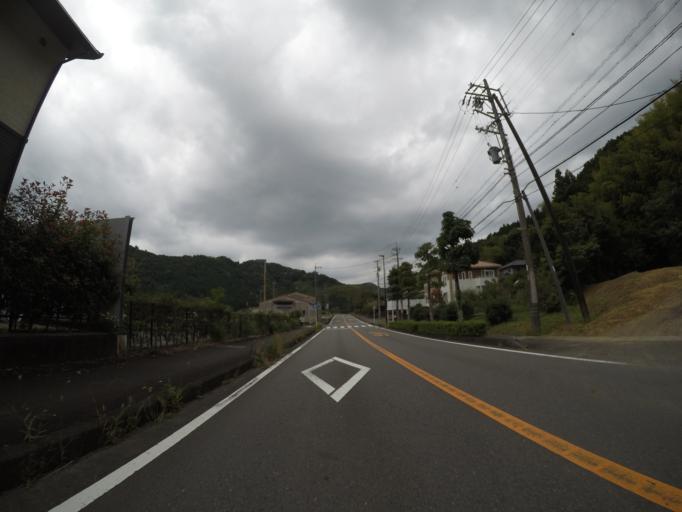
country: JP
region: Shizuoka
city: Fujieda
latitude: 34.8998
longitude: 138.2621
